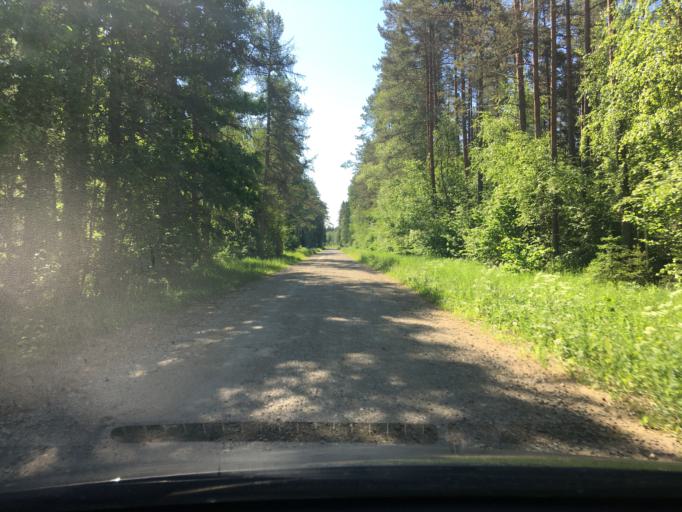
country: EE
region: Laeaene
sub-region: Lihula vald
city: Lihula
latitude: 58.6364
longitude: 23.7957
